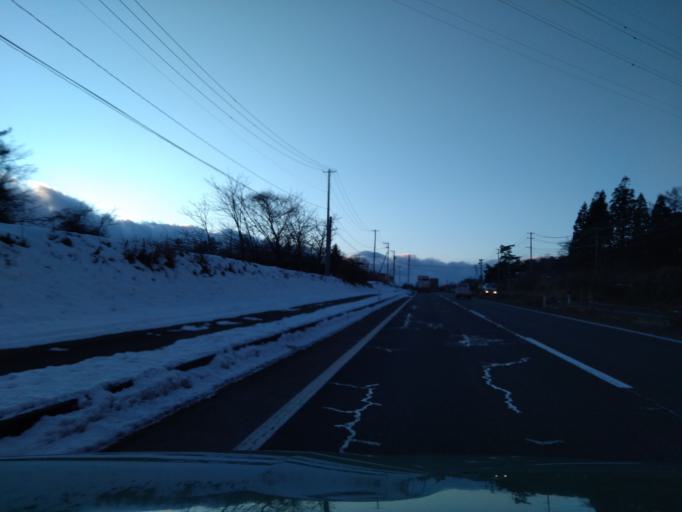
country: JP
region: Iwate
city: Shizukuishi
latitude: 39.7020
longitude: 141.0394
